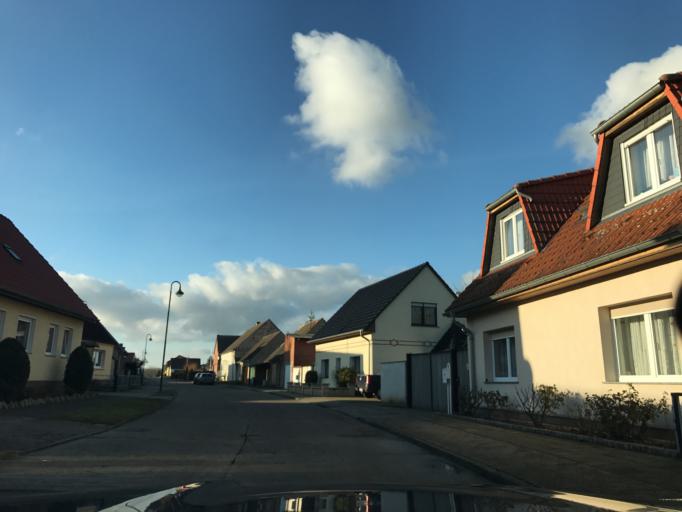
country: DE
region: Saxony-Anhalt
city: Loburg
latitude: 52.1802
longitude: 12.0434
